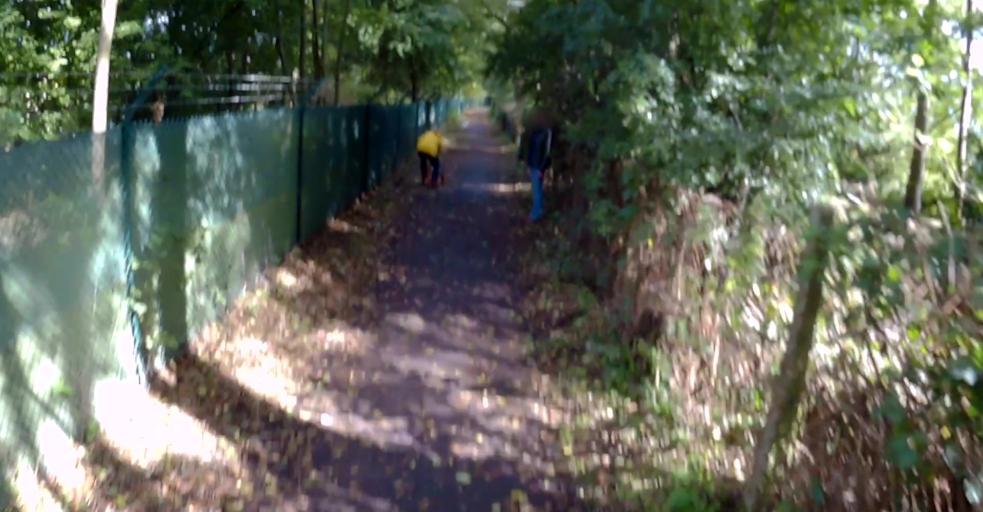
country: GB
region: England
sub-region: Surrey
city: Frimley
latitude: 51.3029
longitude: -0.7381
